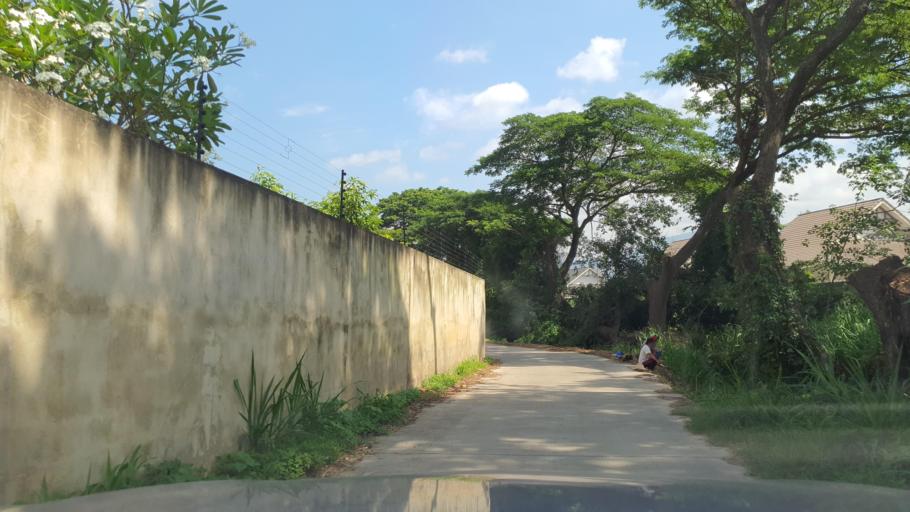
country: TH
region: Chiang Mai
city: Hang Dong
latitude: 18.7187
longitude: 98.9164
